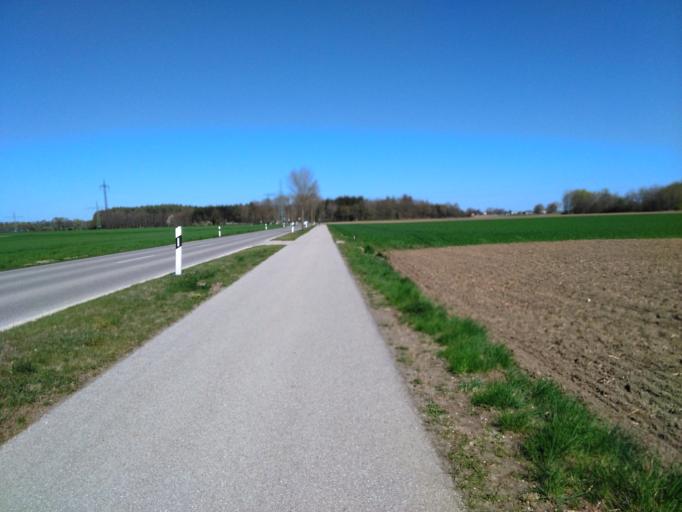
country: DE
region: Bavaria
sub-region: Upper Bavaria
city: Mammendorf
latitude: 48.2105
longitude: 11.1851
